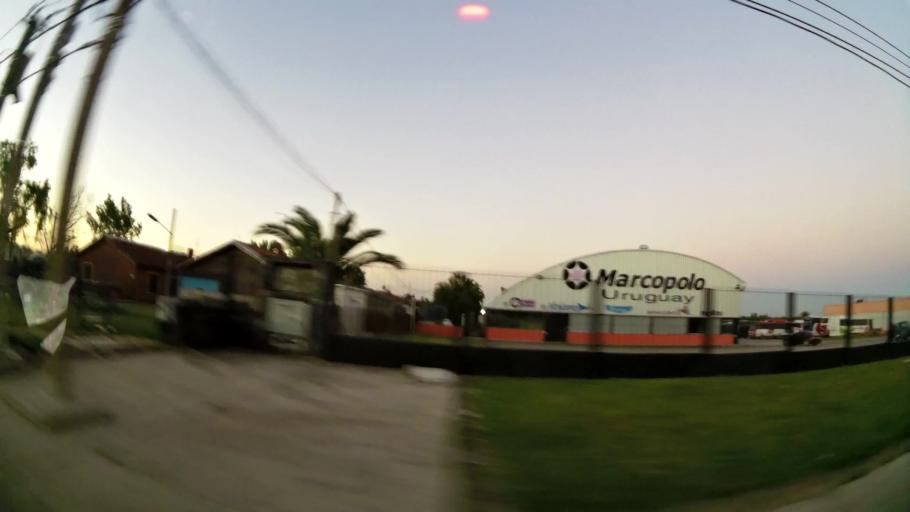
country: UY
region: Montevideo
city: Montevideo
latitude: -34.8216
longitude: -56.1516
